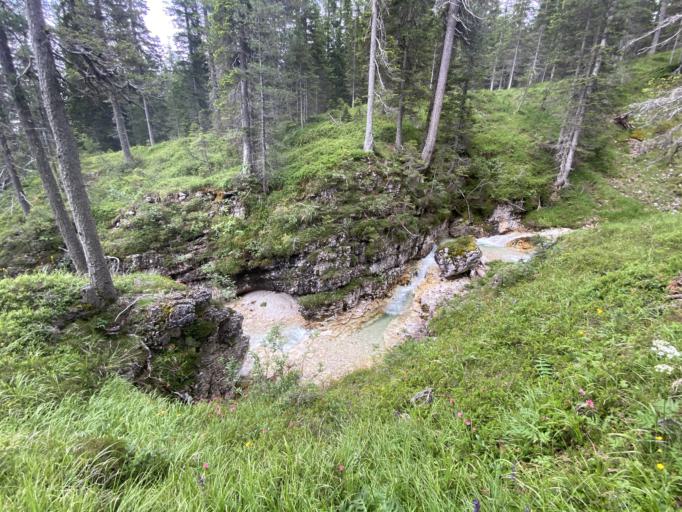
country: IT
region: Veneto
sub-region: Provincia di Belluno
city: Cortina d'Ampezzo
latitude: 46.4940
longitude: 12.1181
